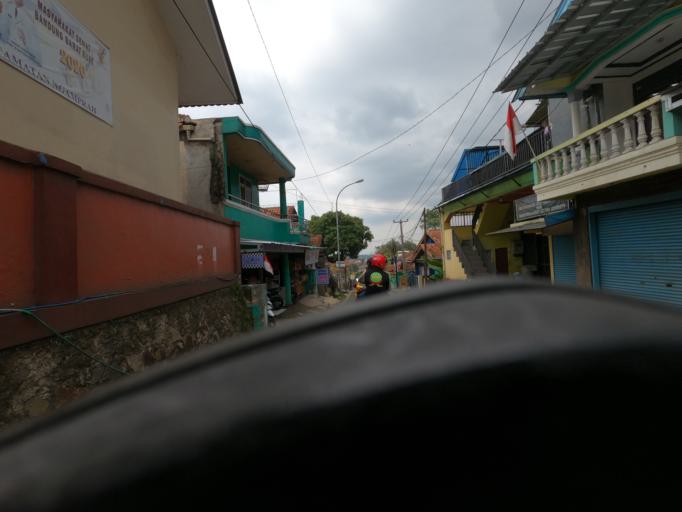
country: ID
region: West Java
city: Padalarang
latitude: -6.8428
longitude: 107.5012
